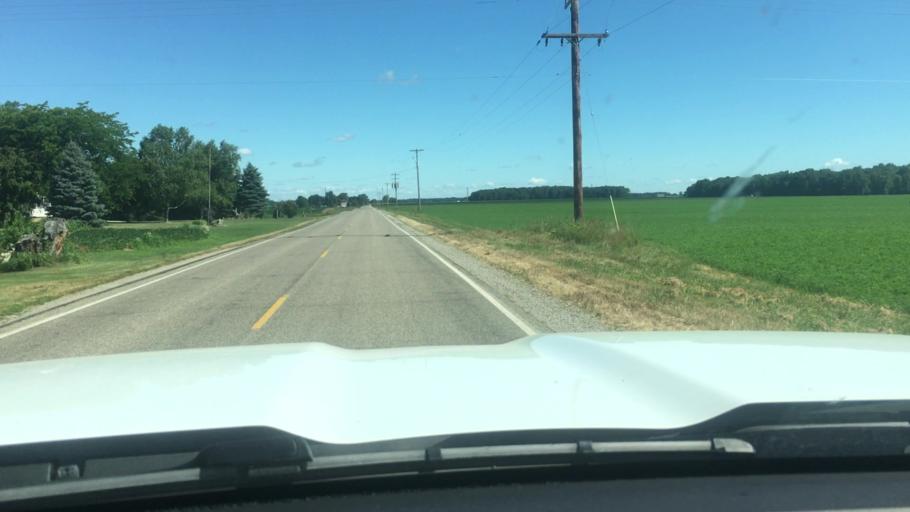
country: US
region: Michigan
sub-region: Montcalm County
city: Carson City
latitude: 43.1916
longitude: -84.7780
